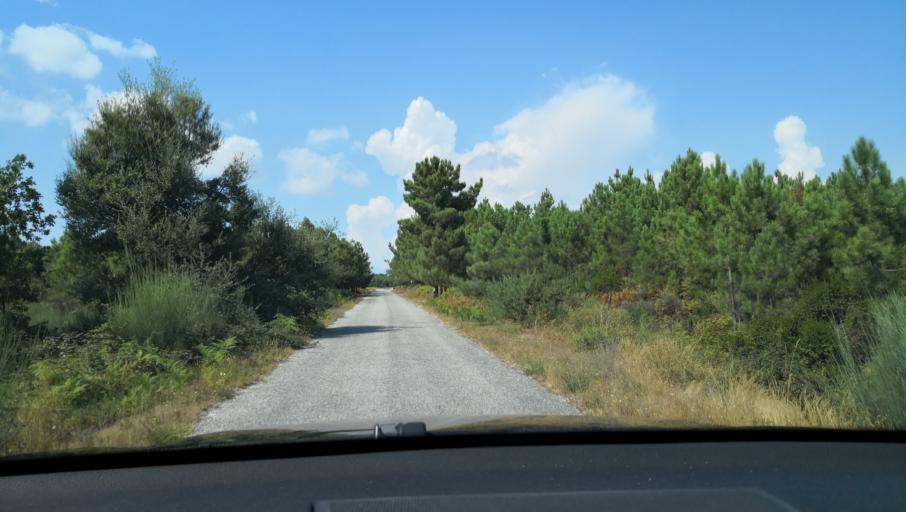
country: PT
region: Vila Real
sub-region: Sabrosa
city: Sabrosa
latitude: 41.3050
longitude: -7.5814
